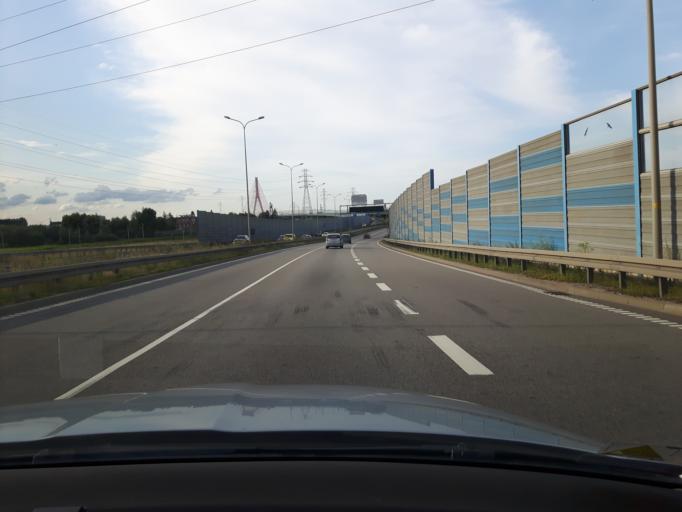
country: PL
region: Pomeranian Voivodeship
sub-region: Gdansk
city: Gdansk
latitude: 54.3446
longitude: 18.6975
